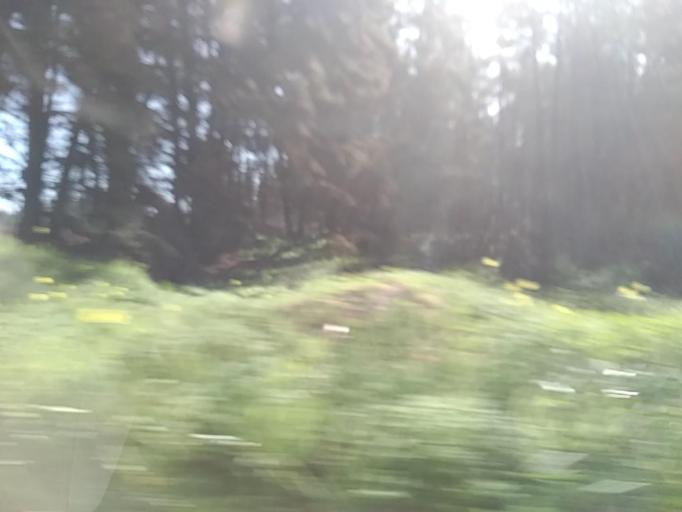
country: CL
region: Valparaiso
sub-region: Provincia de Valparaiso
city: Vina del Mar
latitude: -32.9571
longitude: -71.5238
